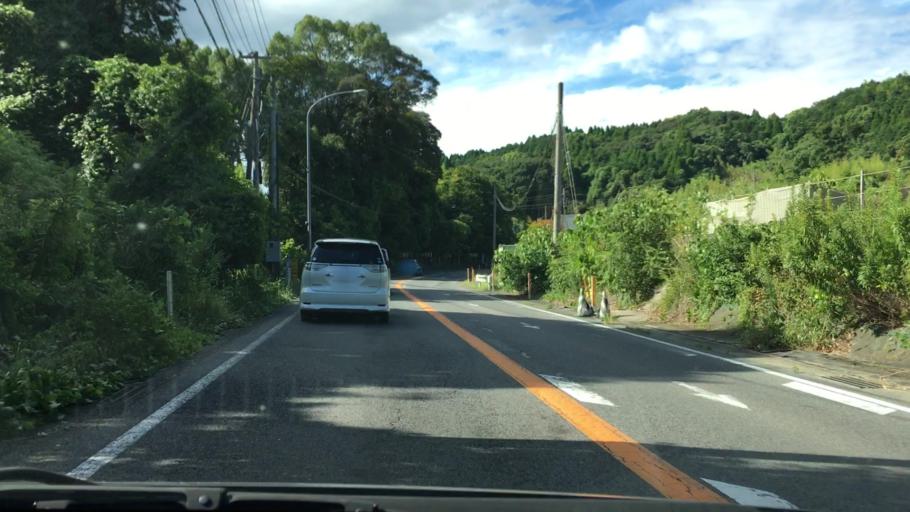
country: JP
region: Saga Prefecture
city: Takeocho-takeo
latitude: 33.1869
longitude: 129.9868
